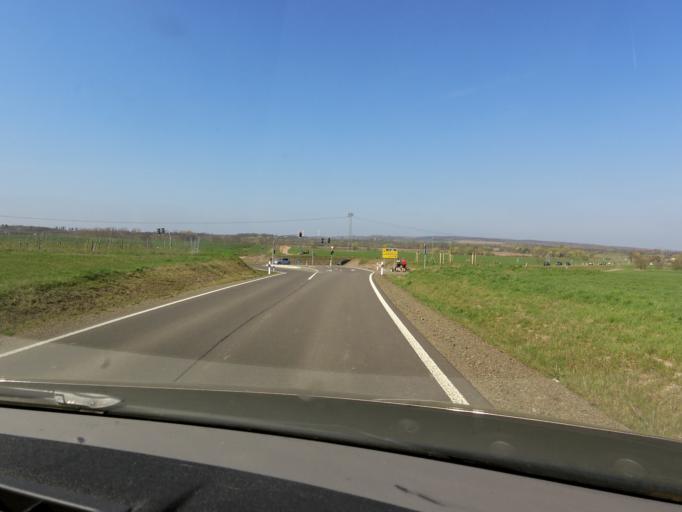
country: DE
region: Thuringia
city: Emleben
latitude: 50.9149
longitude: 10.6514
